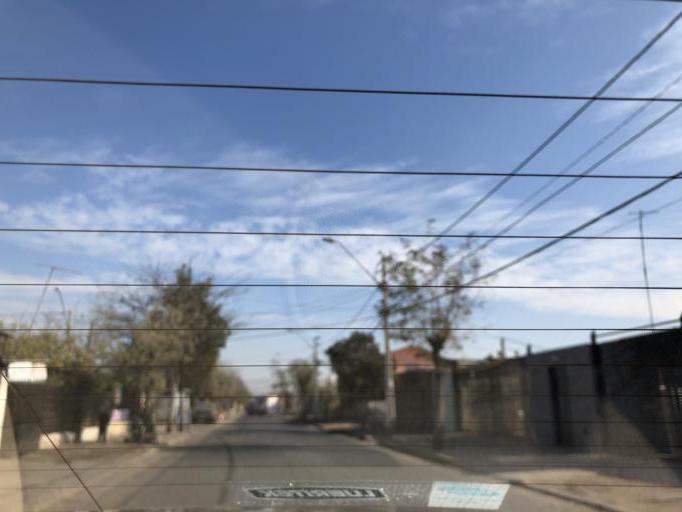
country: CL
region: Santiago Metropolitan
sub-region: Provincia de Cordillera
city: Puente Alto
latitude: -33.6168
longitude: -70.5726
